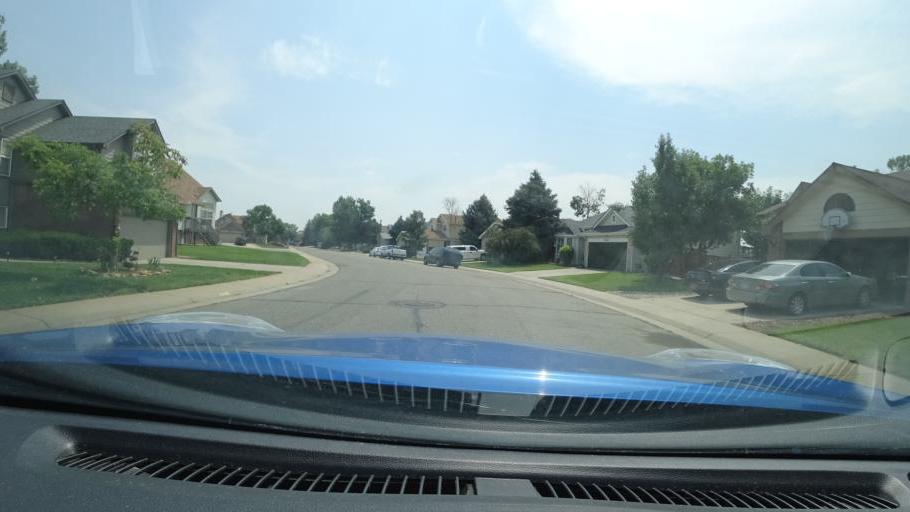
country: US
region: Colorado
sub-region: Adams County
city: Aurora
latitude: 39.7744
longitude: -104.7583
